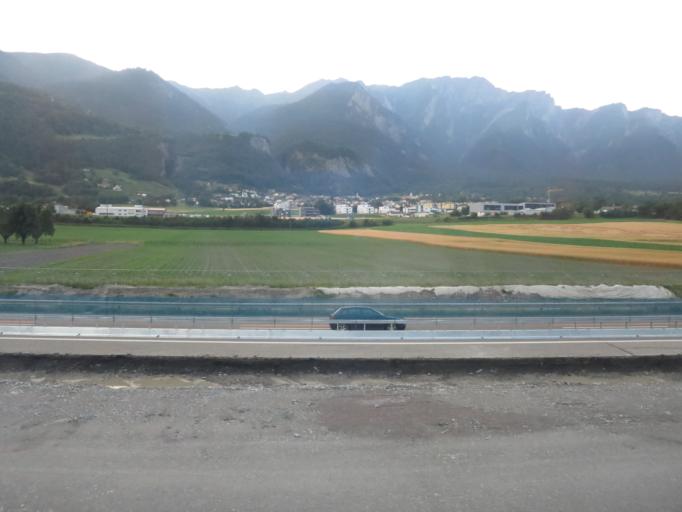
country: CH
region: Grisons
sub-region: Landquart District
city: Trimmis
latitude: 46.9076
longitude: 9.5513
